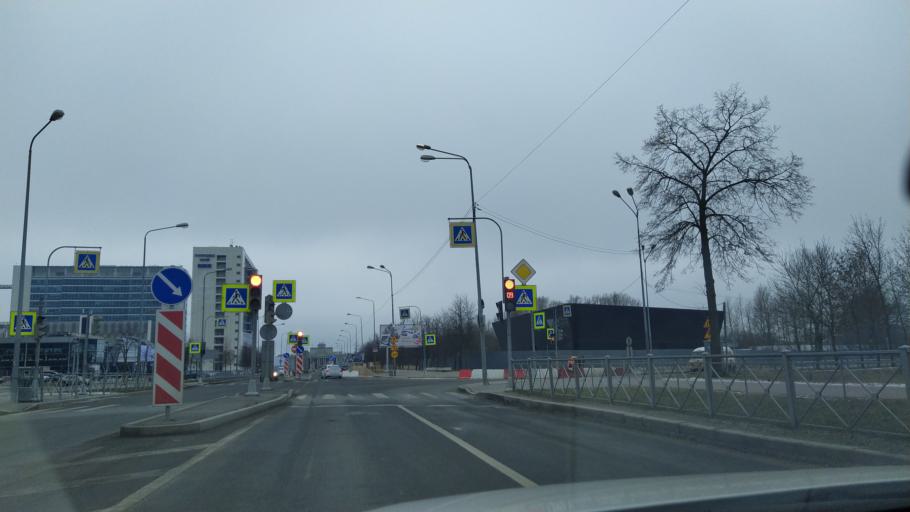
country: RU
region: St.-Petersburg
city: Kupchino
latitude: 59.8087
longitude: 30.3149
